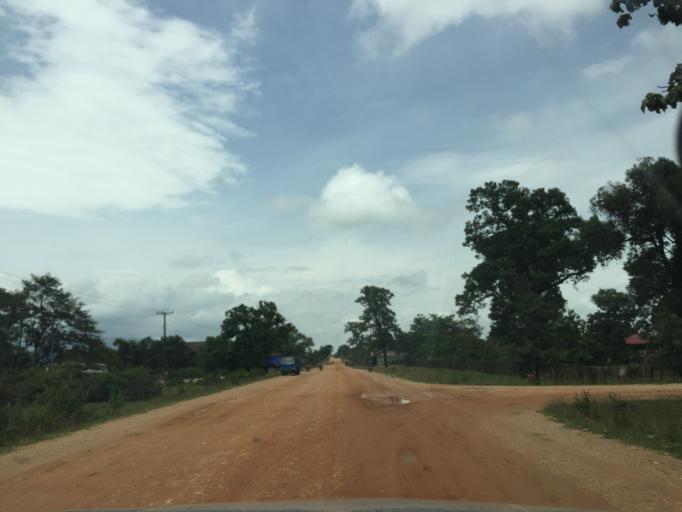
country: LA
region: Attapu
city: Attapu
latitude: 14.6853
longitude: 106.5946
